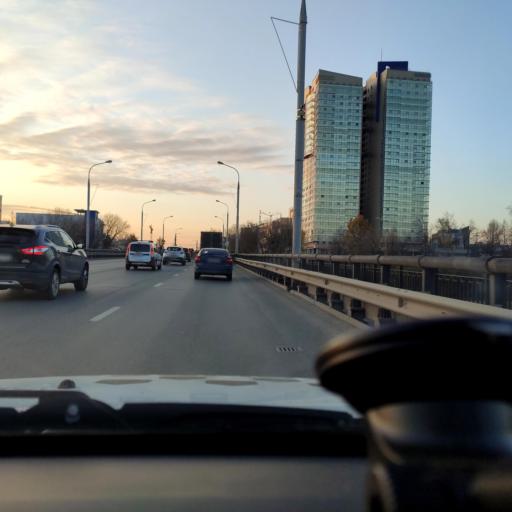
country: RU
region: Perm
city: Perm
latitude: 58.0167
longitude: 56.2226
